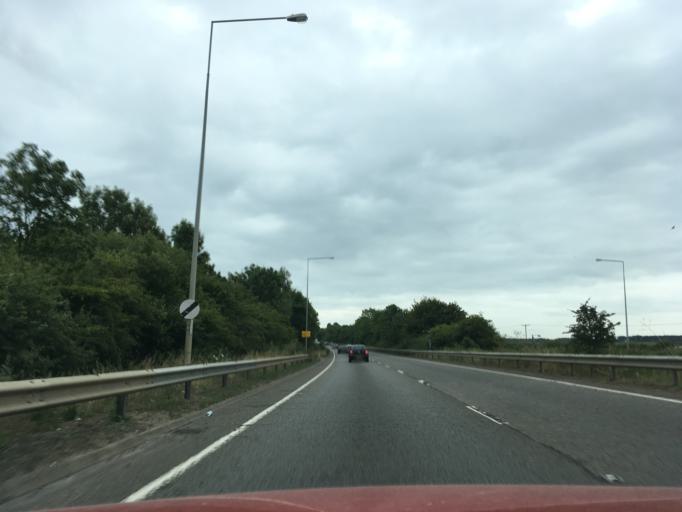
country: GB
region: England
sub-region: Milton Keynes
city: Bow Brickhill
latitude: 51.9899
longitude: -0.6953
